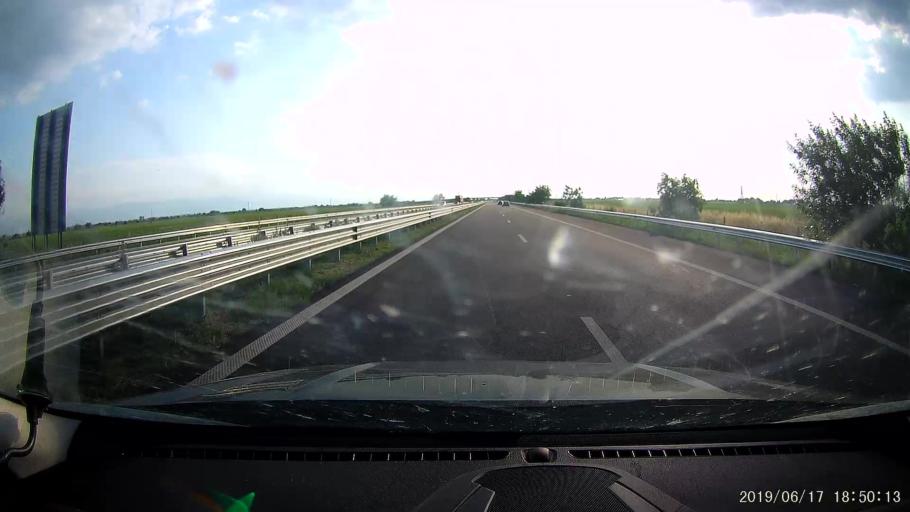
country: BG
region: Plovdiv
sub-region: Obshtina Rakovski
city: Rakovski
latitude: 42.2159
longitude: 25.0072
